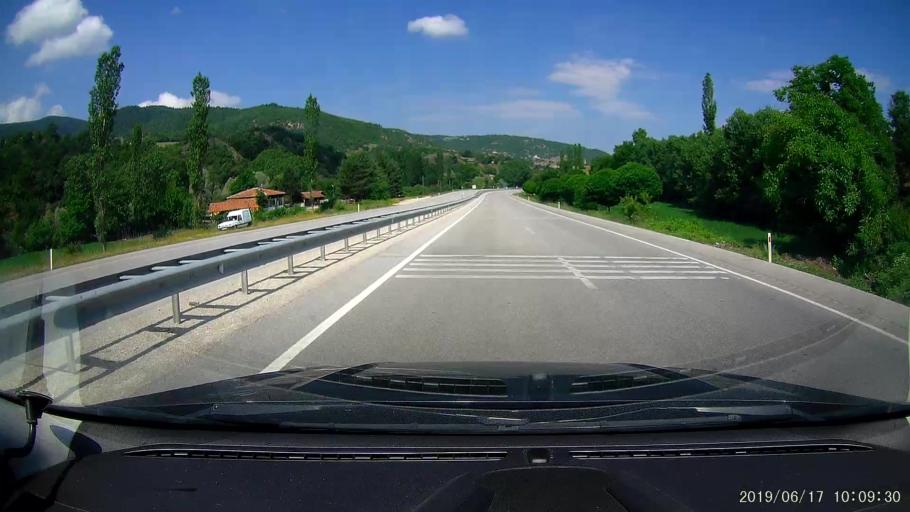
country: TR
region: Amasya
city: Saraycik
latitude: 40.9483
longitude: 35.1192
